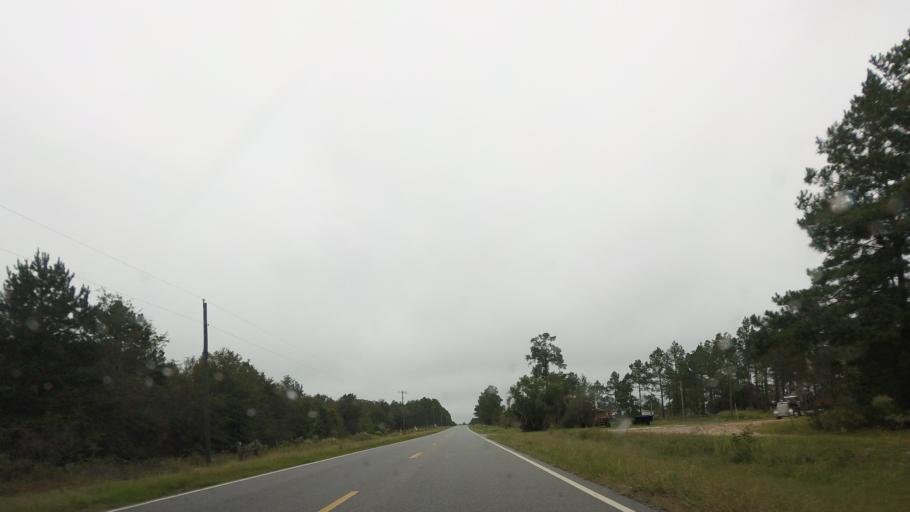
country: US
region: Georgia
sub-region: Berrien County
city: Enigma
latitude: 31.4400
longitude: -83.2408
